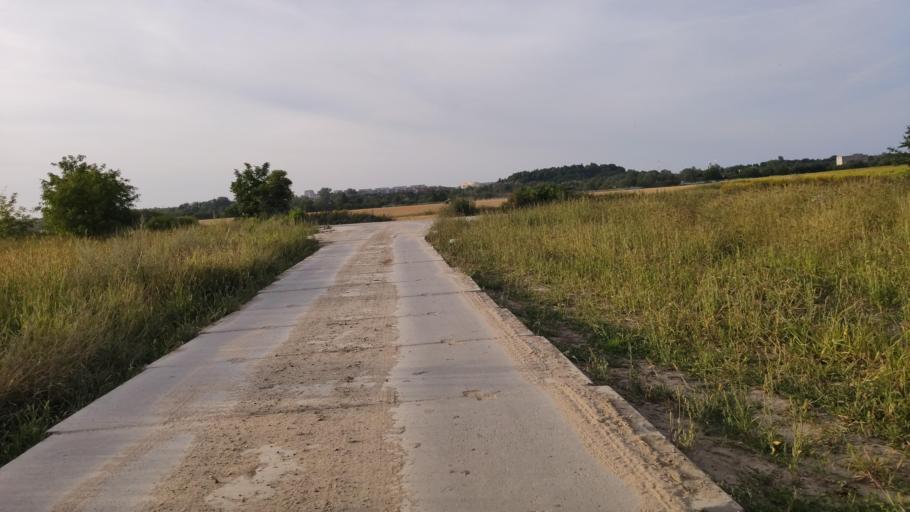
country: PL
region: Lower Silesian Voivodeship
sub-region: Powiat wroclawski
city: Zerniki Wroclawskie
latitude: 51.0622
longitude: 17.0483
